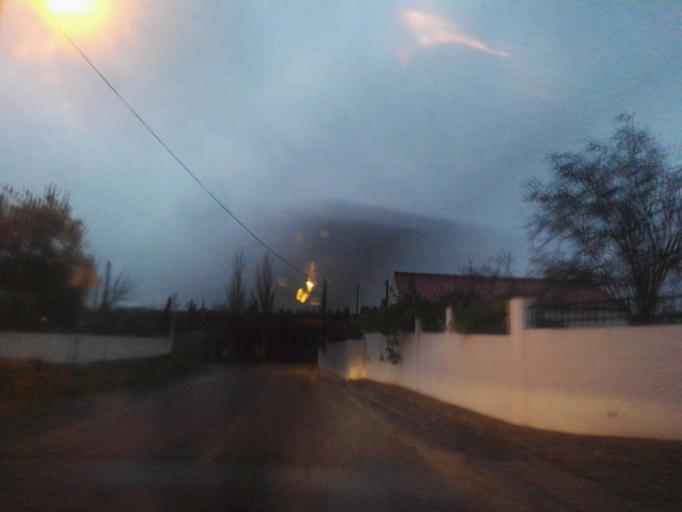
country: PT
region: Santarem
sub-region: Santarem
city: Alcanede
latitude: 39.3111
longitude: -8.7824
